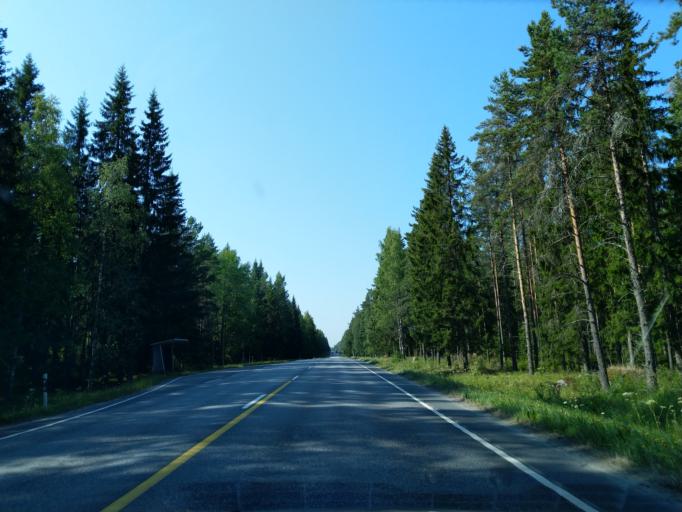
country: FI
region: Satakunta
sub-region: Pori
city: Pomarkku
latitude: 61.6551
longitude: 21.9630
